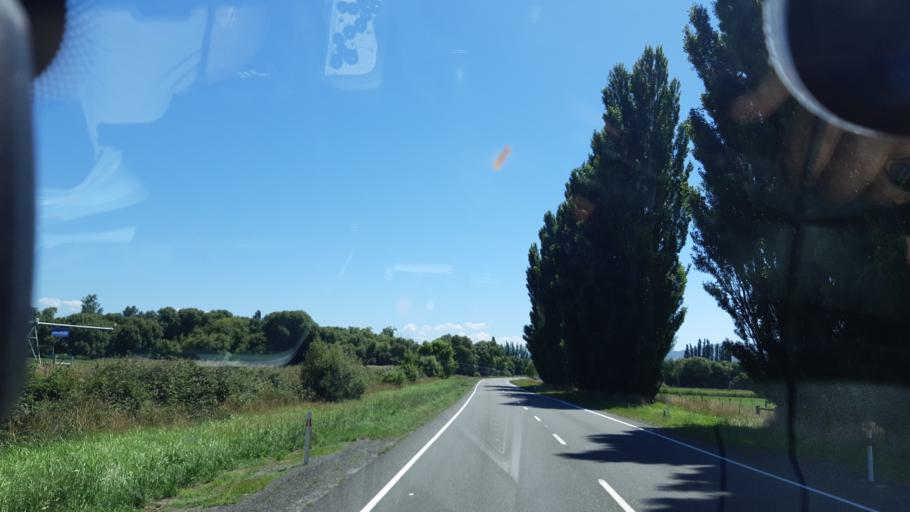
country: NZ
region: Canterbury
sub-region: Kaikoura District
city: Kaikoura
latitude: -42.7323
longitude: 173.2744
